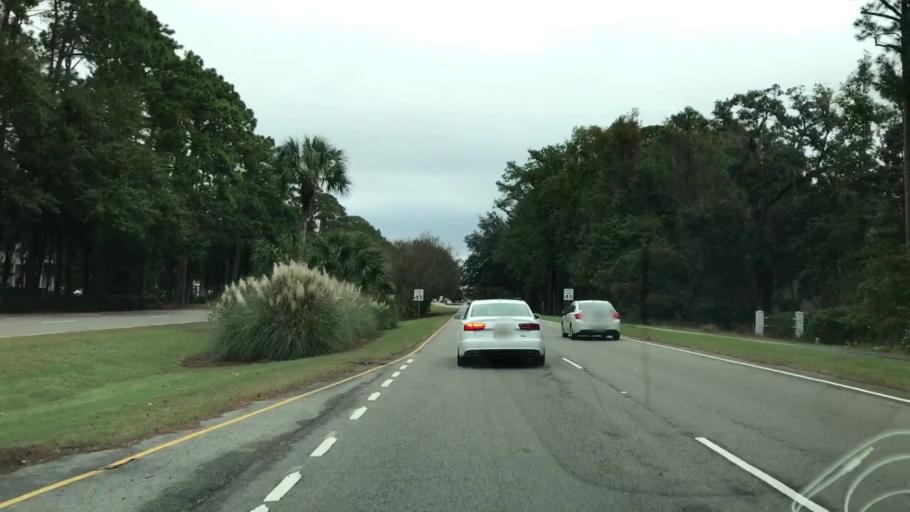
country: US
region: South Carolina
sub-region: Beaufort County
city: Hilton Head Island
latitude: 32.1579
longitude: -80.7558
